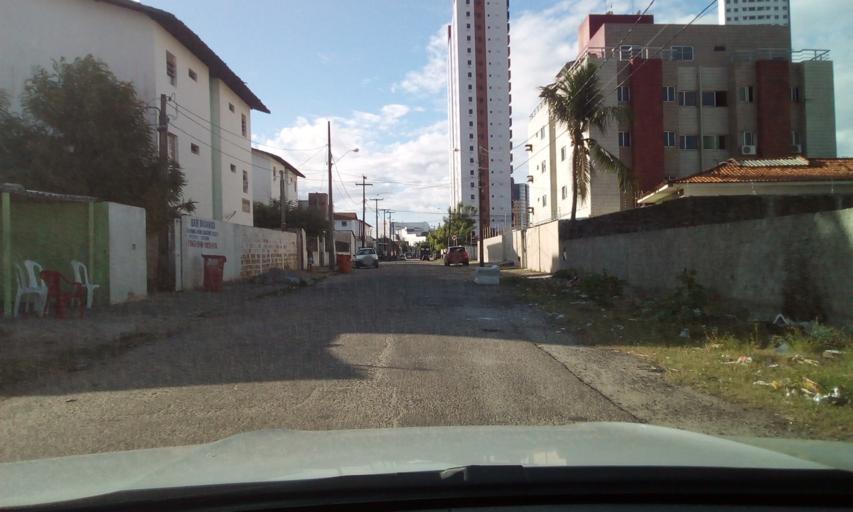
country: BR
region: Paraiba
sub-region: Joao Pessoa
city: Joao Pessoa
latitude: -7.1052
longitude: -34.8413
